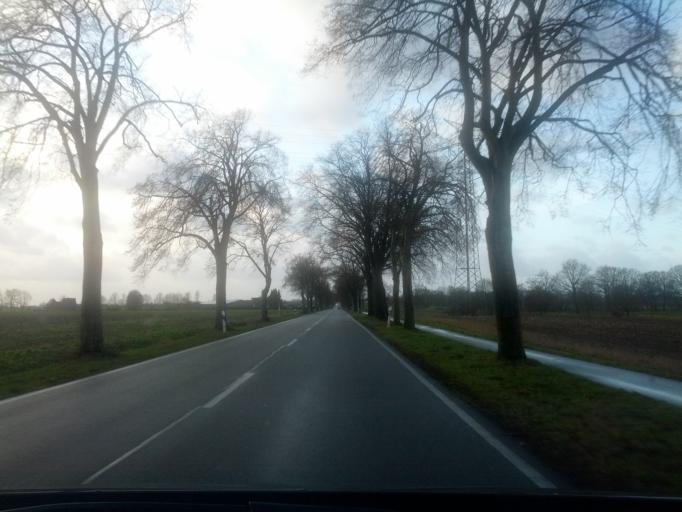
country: DE
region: Lower Saxony
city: Sittensen
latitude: 53.2667
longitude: 9.4960
